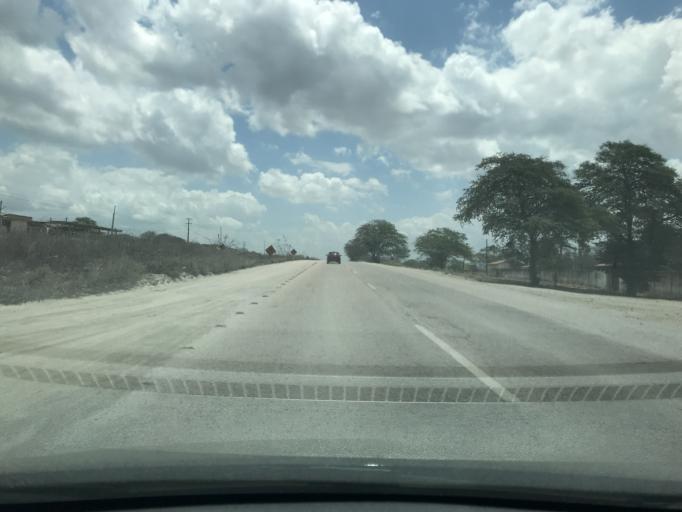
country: BR
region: Pernambuco
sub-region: Caruaru
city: Caruaru
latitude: -8.2956
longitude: -35.8900
